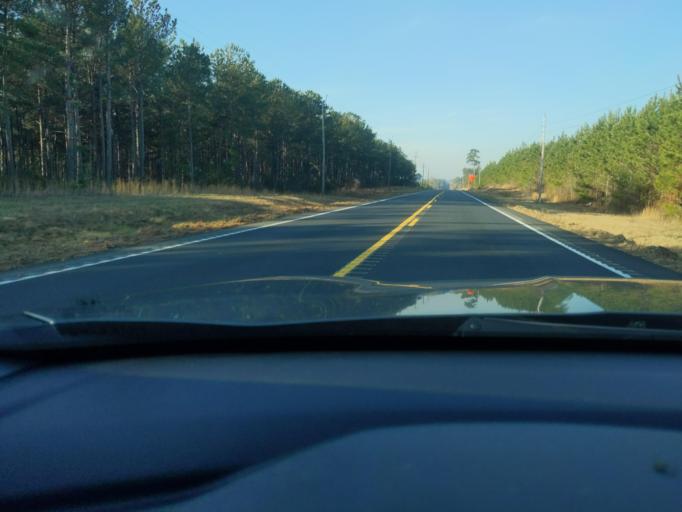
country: US
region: South Carolina
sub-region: Greenwood County
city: Ninety Six
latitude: 34.2047
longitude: -81.8200
